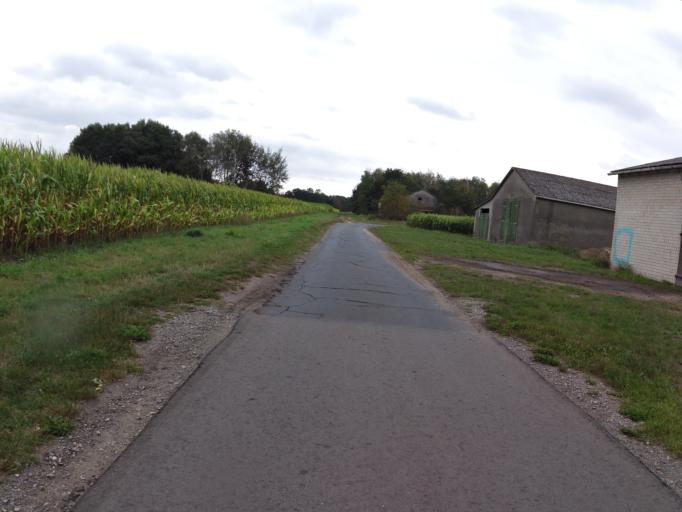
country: DE
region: Lower Saxony
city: Scheessel
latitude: 53.1565
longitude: 9.4558
